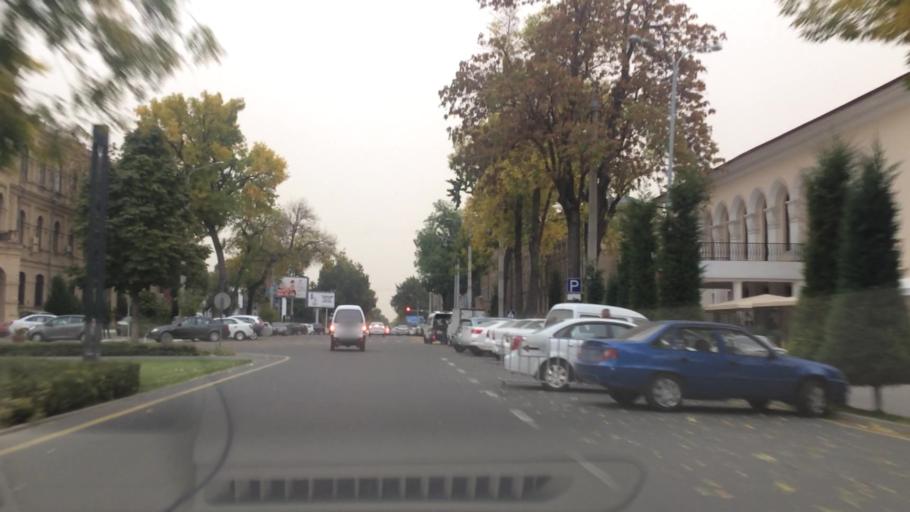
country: UZ
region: Toshkent Shahri
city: Tashkent
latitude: 41.3084
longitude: 69.2825
